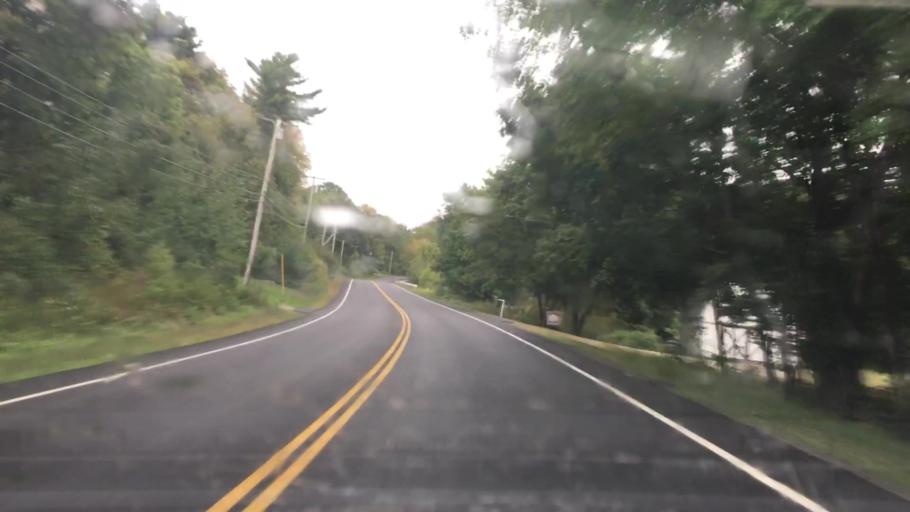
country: US
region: Maine
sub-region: Penobscot County
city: Orrington
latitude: 44.6832
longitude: -68.8100
